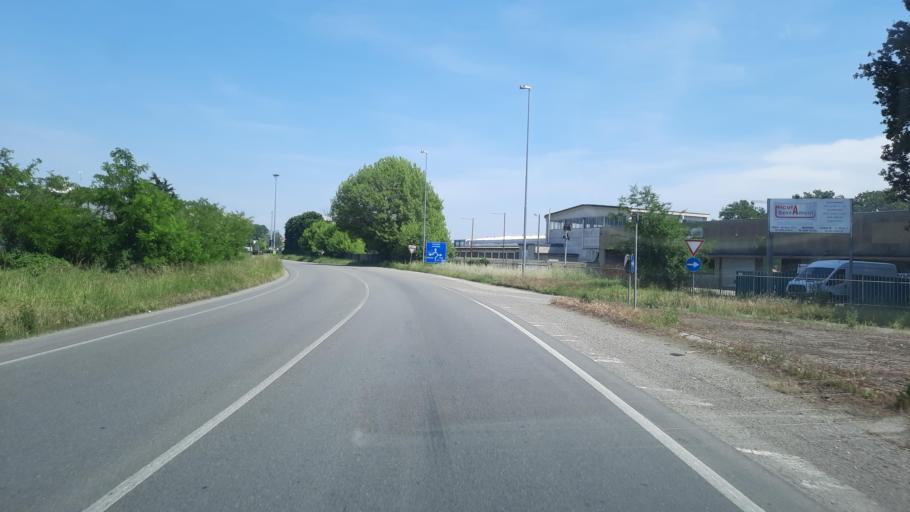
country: IT
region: Lombardy
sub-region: Provincia di Pavia
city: Mortara
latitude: 45.2421
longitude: 8.7428
